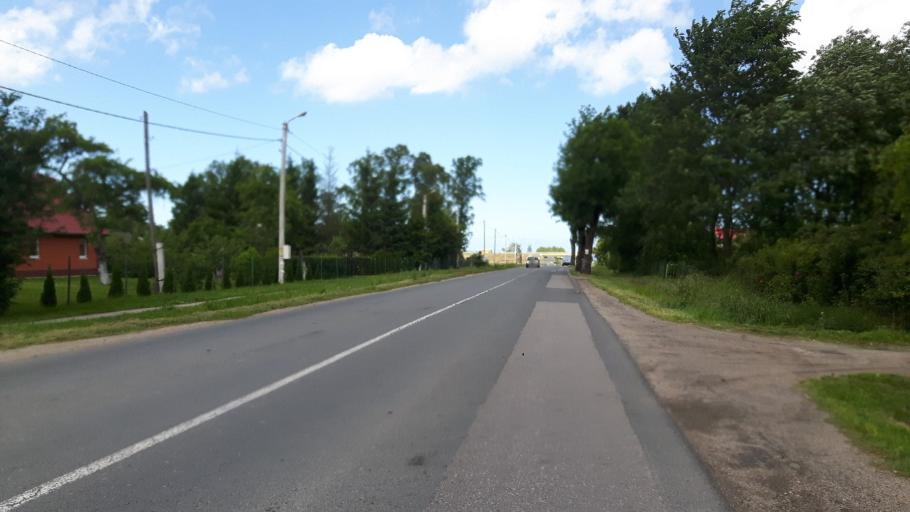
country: RU
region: Kaliningrad
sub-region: Zelenogradskiy Rayon
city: Zelenogradsk
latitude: 54.9190
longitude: 20.3994
